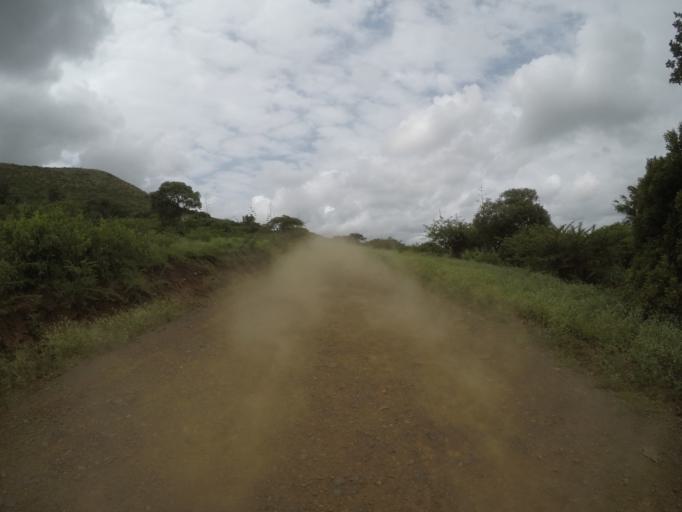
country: ZA
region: KwaZulu-Natal
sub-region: uThungulu District Municipality
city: Empangeni
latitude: -28.6033
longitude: 31.8939
